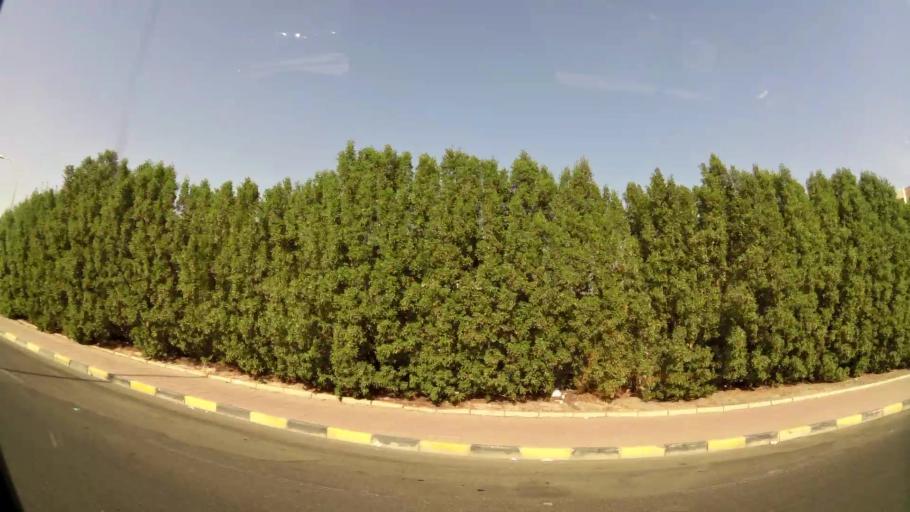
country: KW
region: Muhafazat Hawalli
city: As Salimiyah
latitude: 29.3285
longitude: 48.0832
